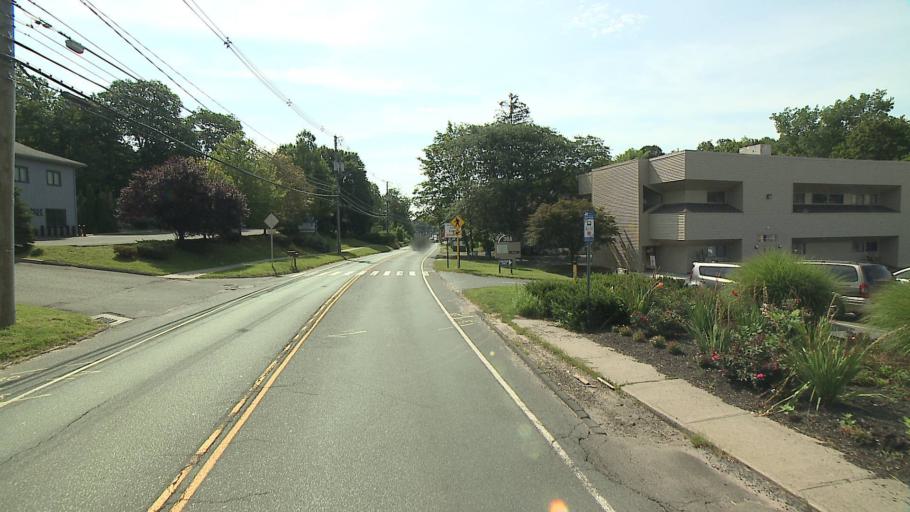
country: US
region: Connecticut
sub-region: Fairfield County
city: Danbury
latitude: 41.4164
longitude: -73.4616
